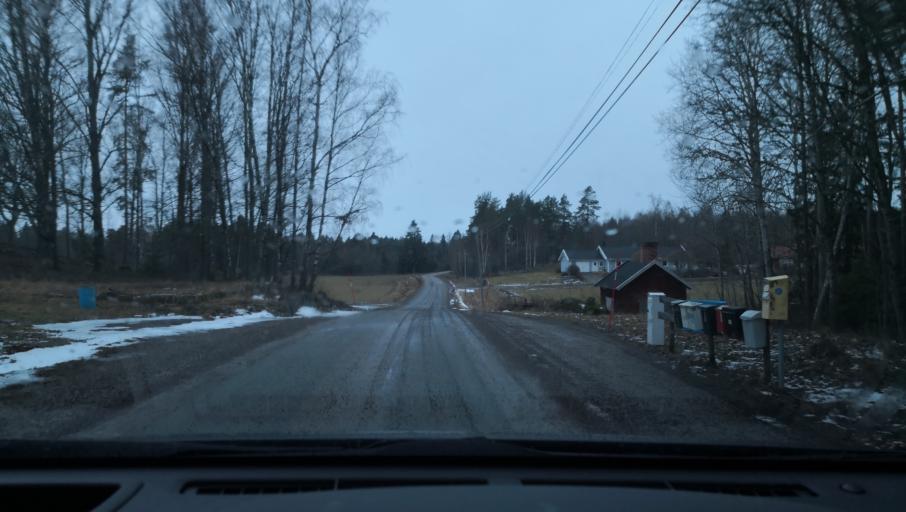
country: SE
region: Uppsala
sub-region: Enkopings Kommun
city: Hummelsta
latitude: 59.4571
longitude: 16.8499
